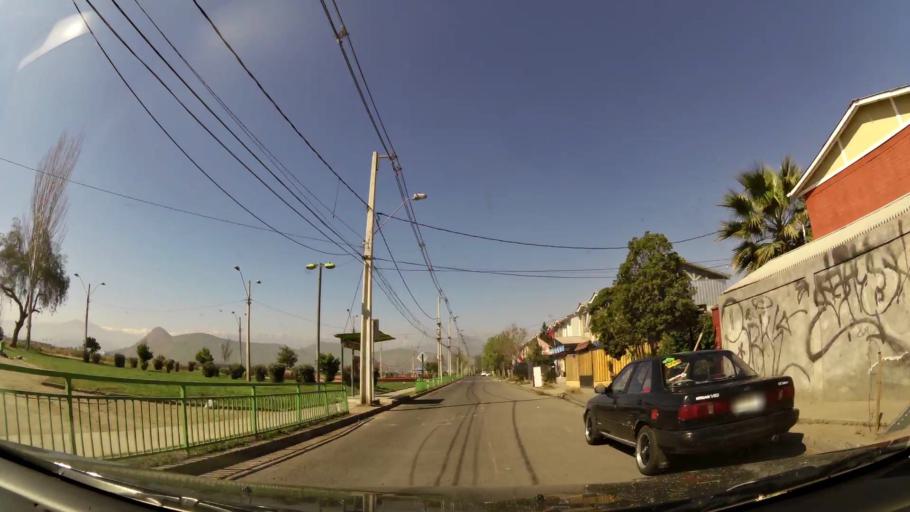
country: CL
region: Santiago Metropolitan
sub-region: Provincia de Santiago
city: Lo Prado
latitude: -33.3488
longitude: -70.7379
